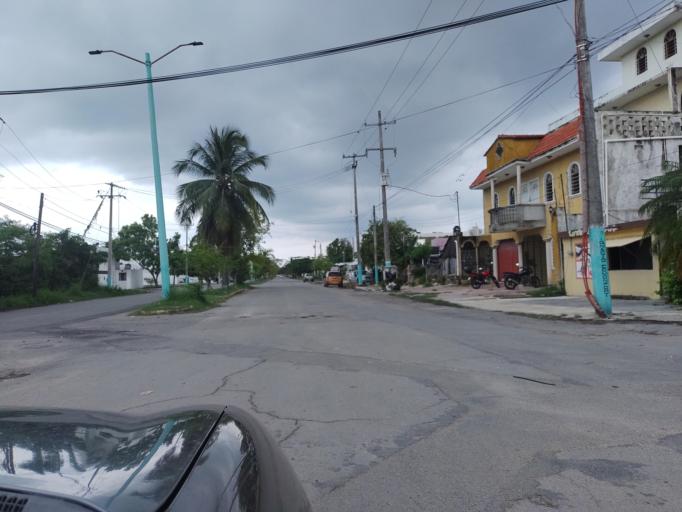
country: MX
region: Quintana Roo
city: Chetumal
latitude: 18.5224
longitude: -88.2744
